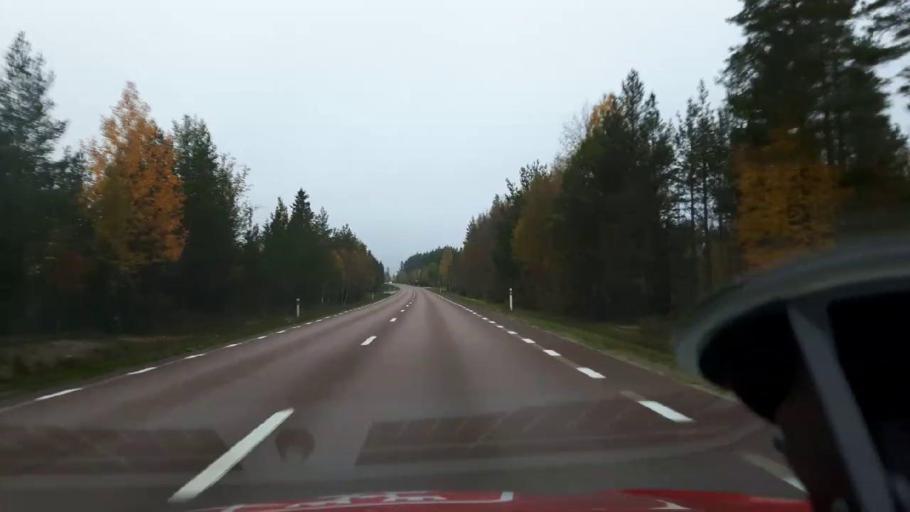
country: SE
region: Jaemtland
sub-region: Bergs Kommun
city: Hoverberg
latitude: 62.5410
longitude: 14.4502
